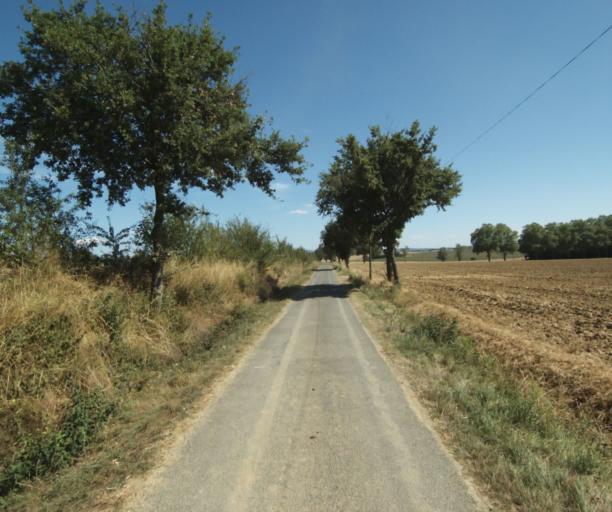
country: FR
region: Midi-Pyrenees
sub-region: Departement de la Haute-Garonne
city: Saint-Felix-Lauragais
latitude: 43.5168
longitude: 1.9010
